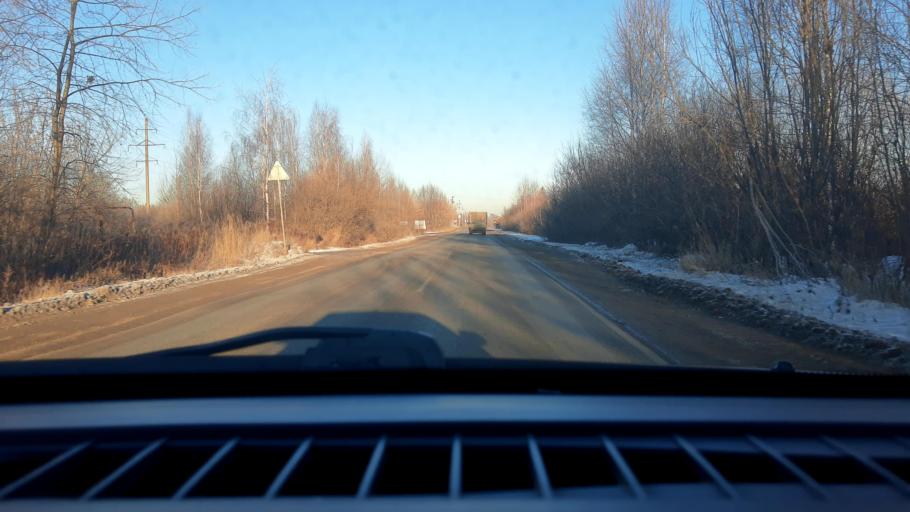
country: RU
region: Nizjnij Novgorod
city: Bor
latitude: 56.3705
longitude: 44.0844
